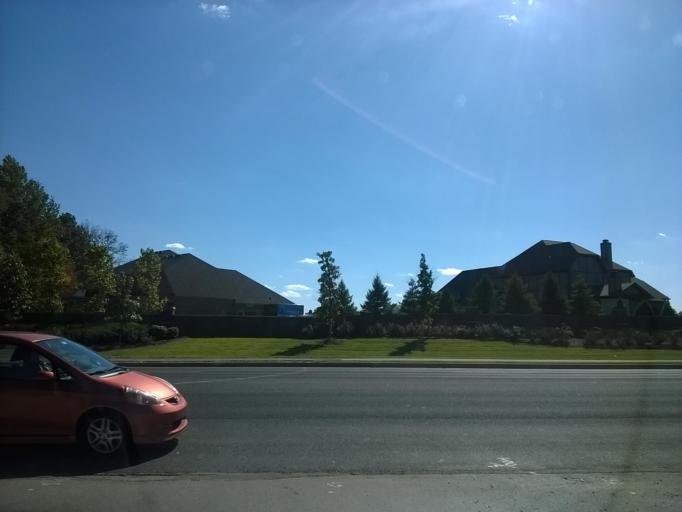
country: US
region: Indiana
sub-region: Hamilton County
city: Carmel
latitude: 40.0004
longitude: -86.0759
